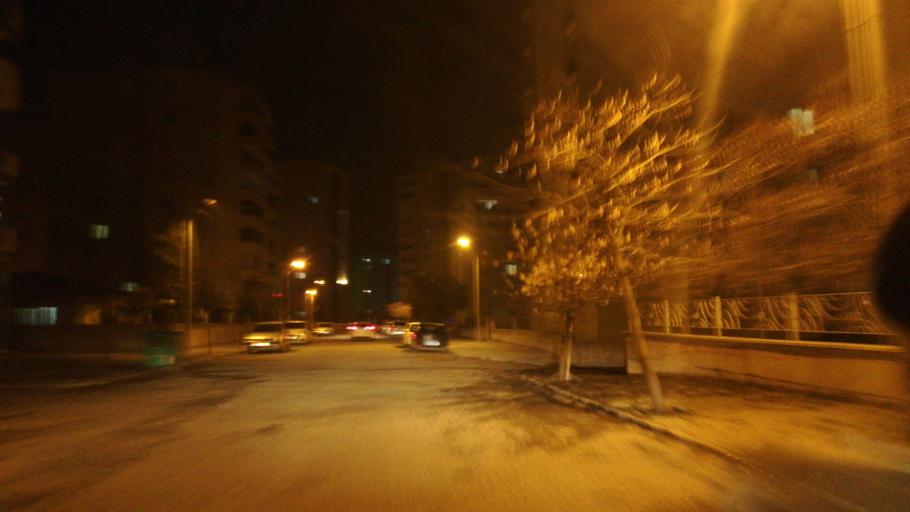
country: TR
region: Kahramanmaras
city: Kahramanmaras
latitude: 37.5972
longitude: 36.8863
